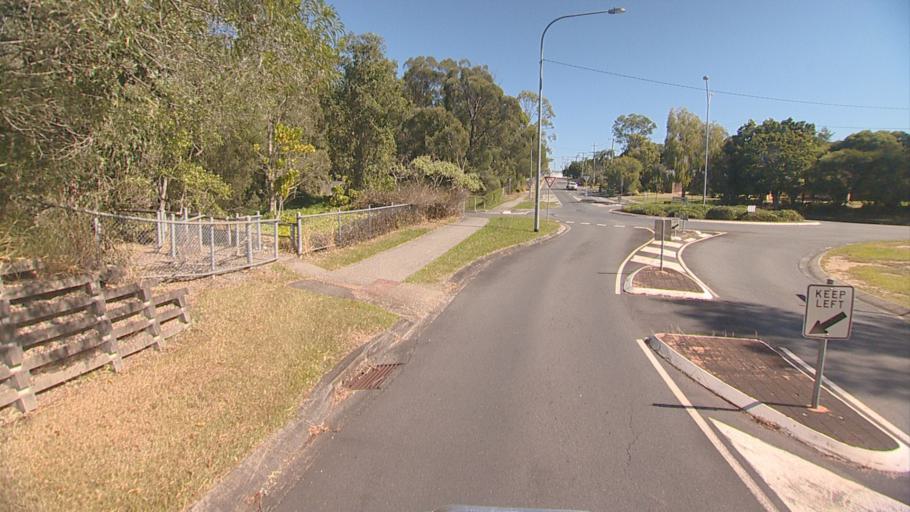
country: AU
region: Queensland
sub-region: Logan
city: Springwood
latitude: -27.6094
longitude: 153.1370
